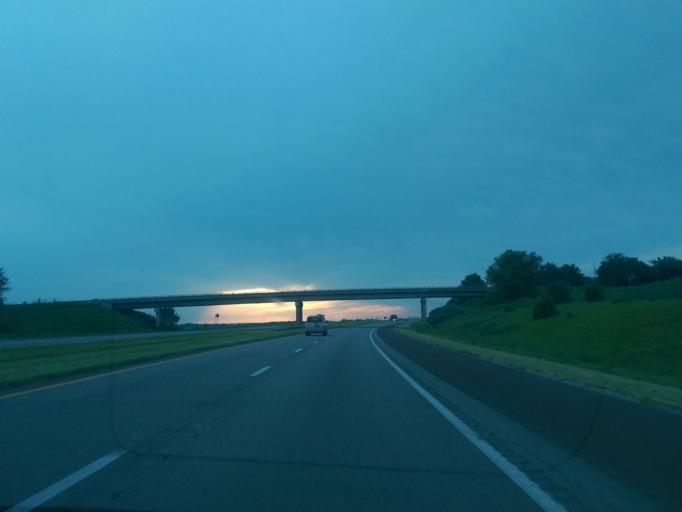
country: US
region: Missouri
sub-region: Holt County
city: Mound City
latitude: 40.1584
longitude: -95.2742
